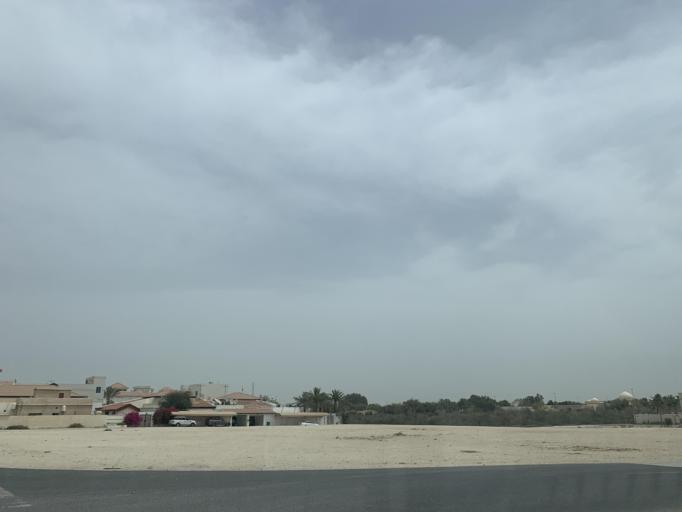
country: BH
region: Northern
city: Ar Rifa'
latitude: 26.1345
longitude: 50.5398
